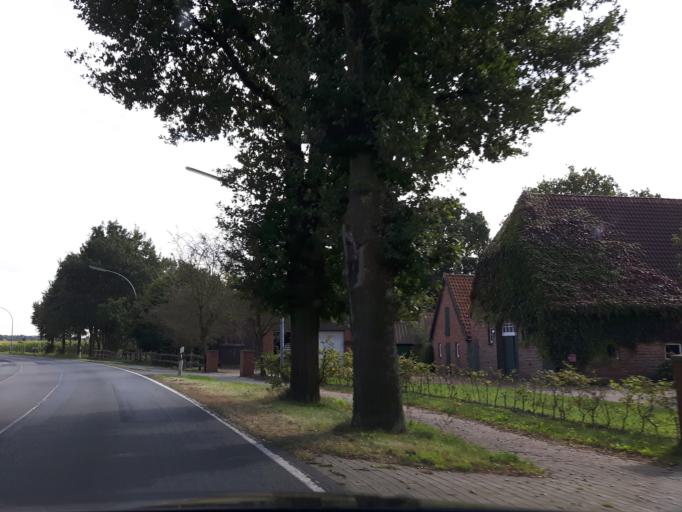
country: DE
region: Lower Saxony
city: Hatten
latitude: 53.0480
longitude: 8.3519
